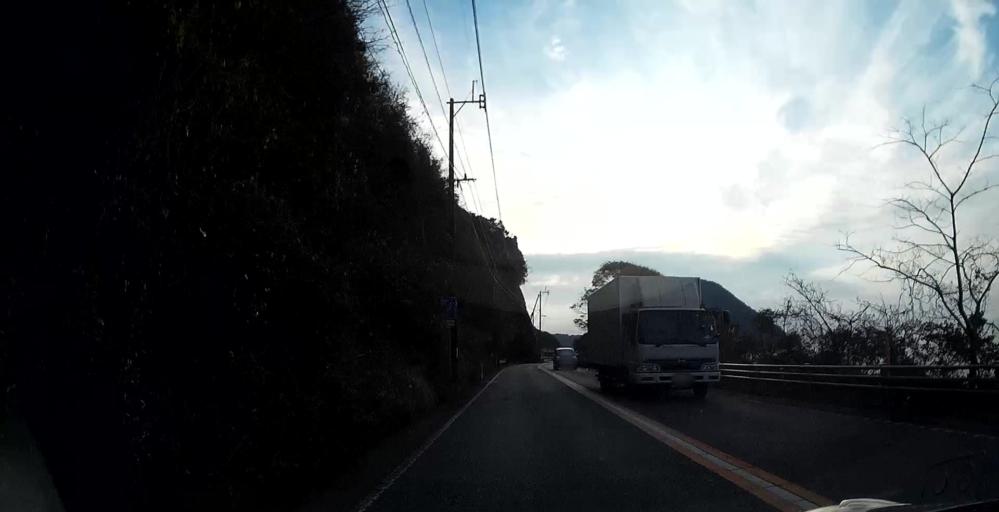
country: JP
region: Nagasaki
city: Shimabara
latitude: 32.6316
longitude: 130.4592
